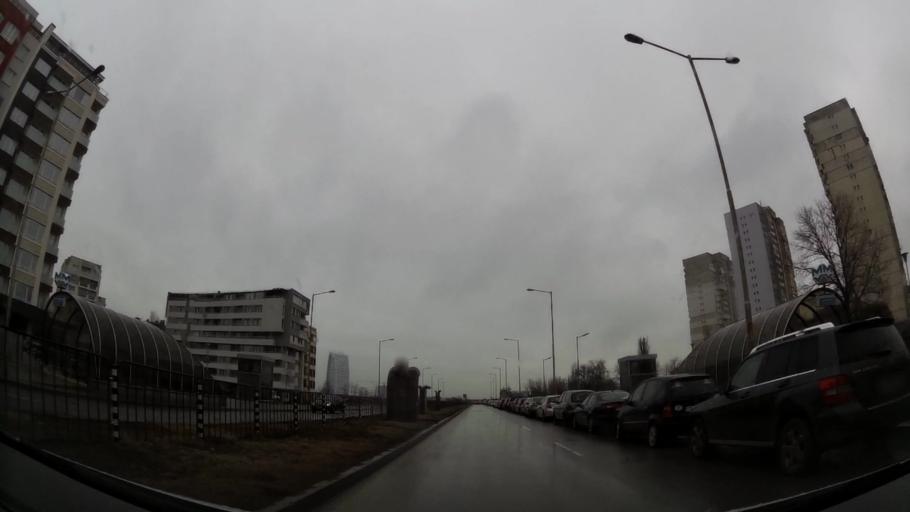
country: BG
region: Sofia-Capital
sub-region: Stolichna Obshtina
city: Sofia
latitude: 42.6468
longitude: 23.3824
